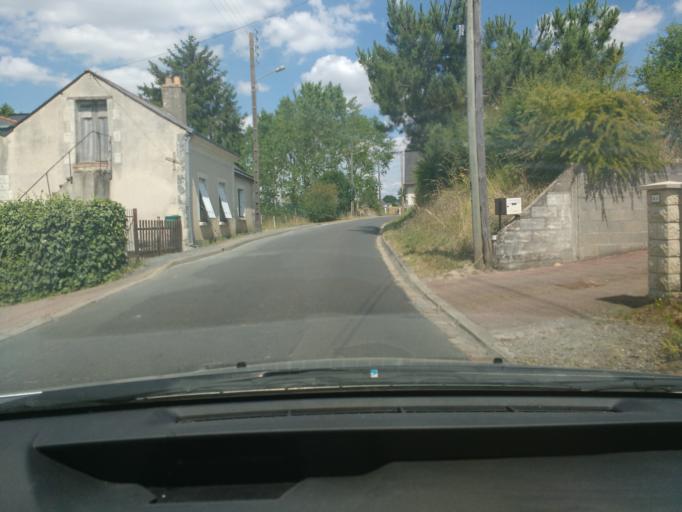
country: FR
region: Pays de la Loire
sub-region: Departement de Maine-et-Loire
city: Bauge-en-Anjou
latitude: 47.5415
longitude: -0.0970
